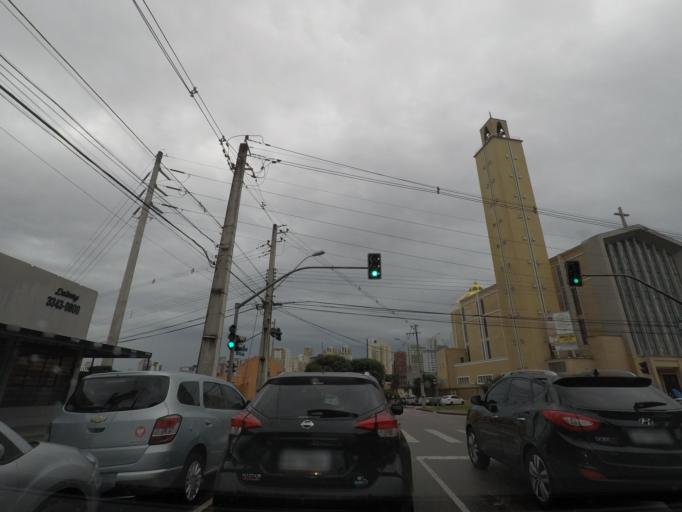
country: BR
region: Parana
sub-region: Curitiba
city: Curitiba
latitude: -25.4531
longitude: -49.2804
